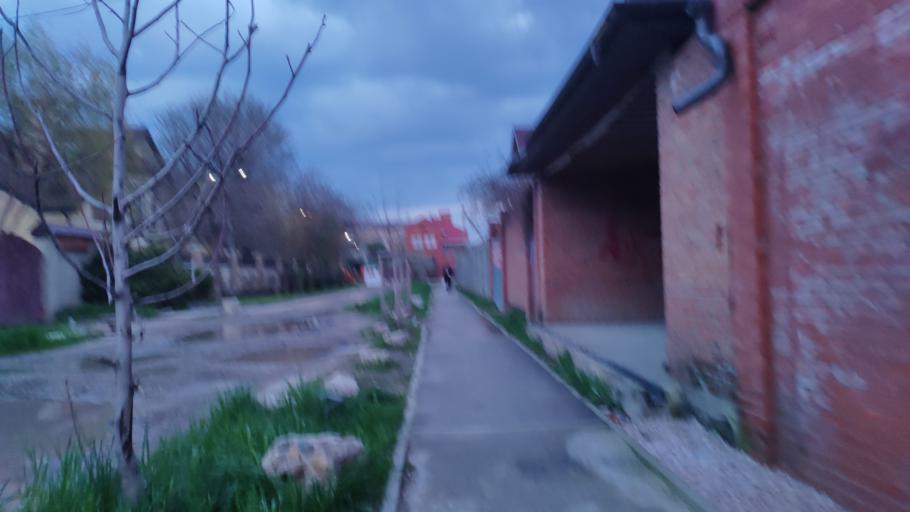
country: RU
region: Krasnodarskiy
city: Krasnodar
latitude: 45.0840
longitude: 39.0065
